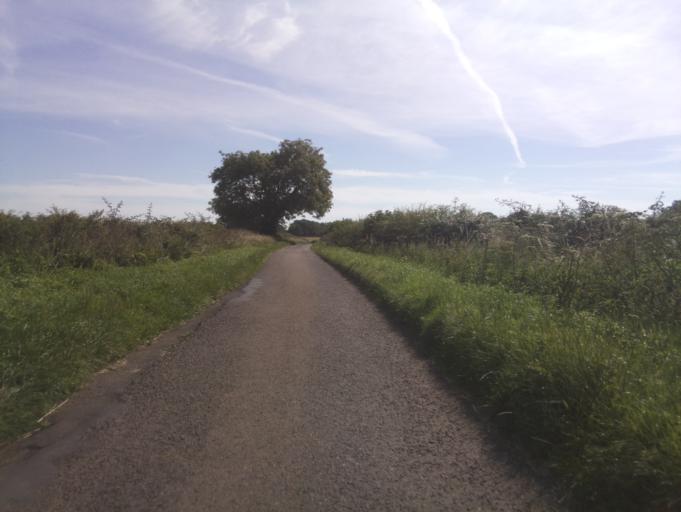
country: GB
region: England
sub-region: Wiltshire
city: Nettleton
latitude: 51.5035
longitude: -2.2543
